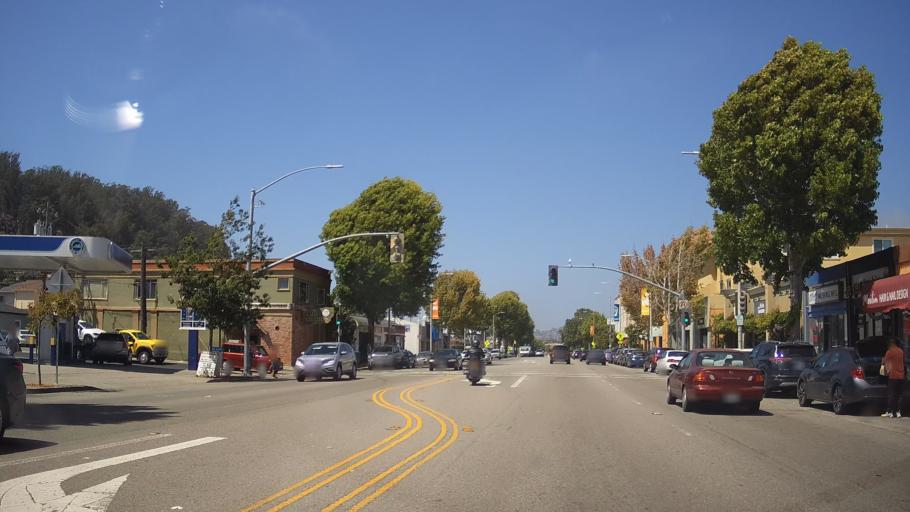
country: US
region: California
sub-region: Alameda County
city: Albany
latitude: 37.8917
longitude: -122.2994
